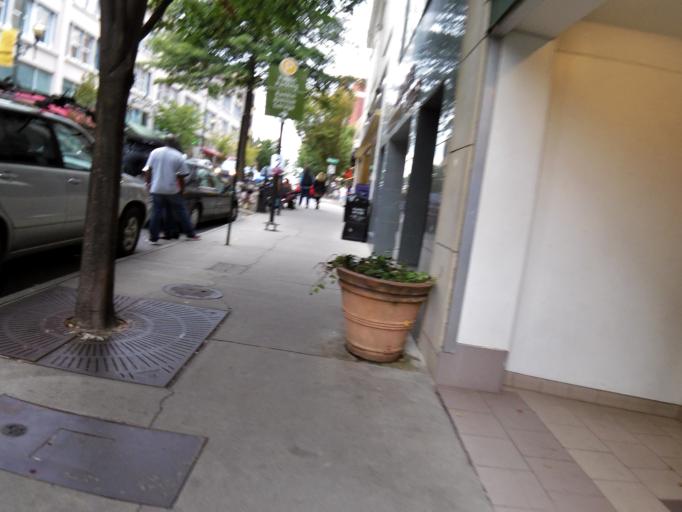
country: US
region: North Carolina
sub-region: Buncombe County
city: Asheville
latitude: 35.5958
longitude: -82.5547
